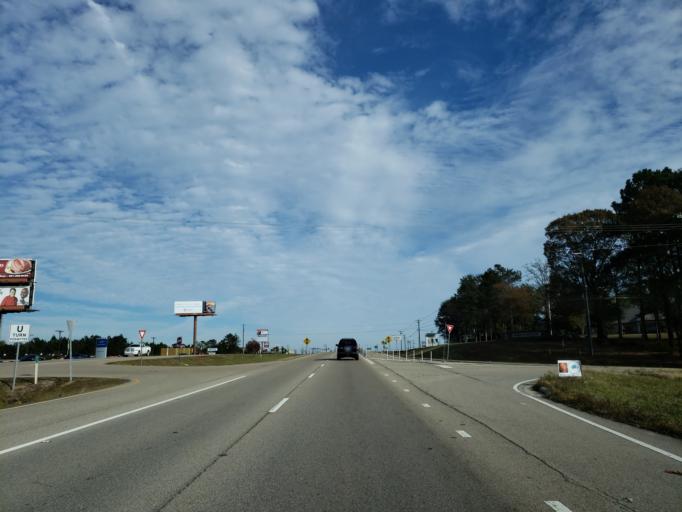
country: US
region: Mississippi
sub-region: Lamar County
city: West Hattiesburg
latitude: 31.3173
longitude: -89.4179
